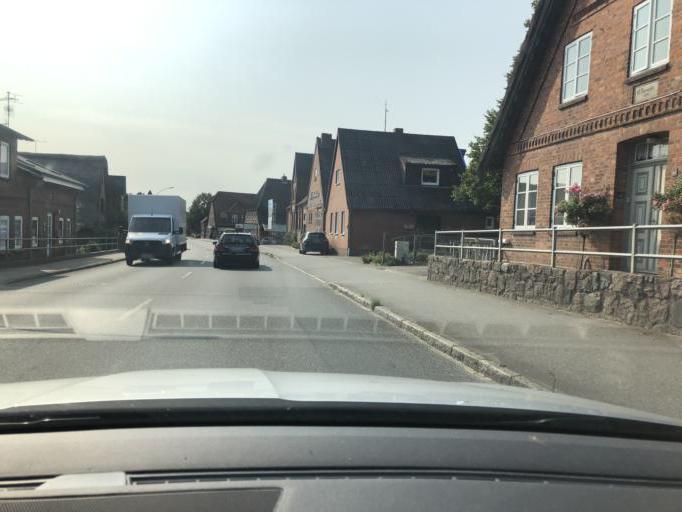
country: DE
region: Schleswig-Holstein
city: Gross Gronau
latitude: 53.8032
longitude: 10.7501
